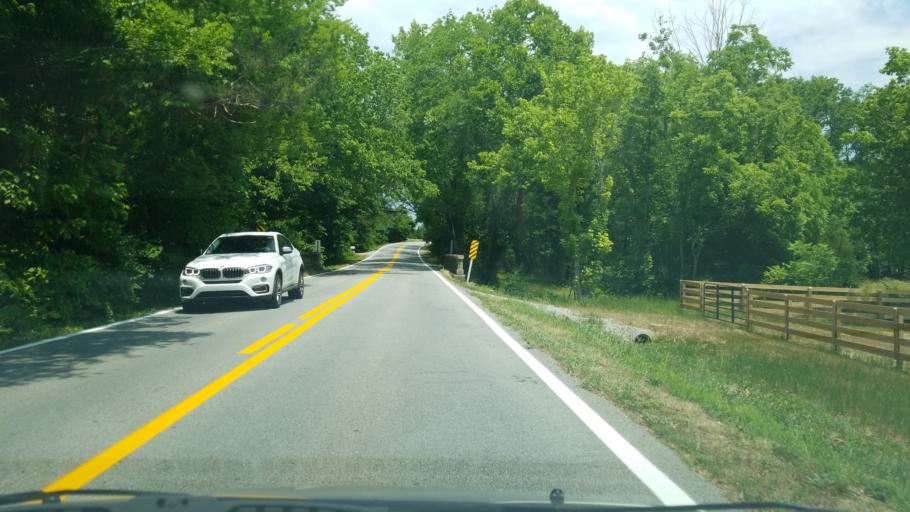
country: US
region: Tennessee
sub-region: Hamilton County
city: East Brainerd
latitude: 34.9908
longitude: -85.0965
